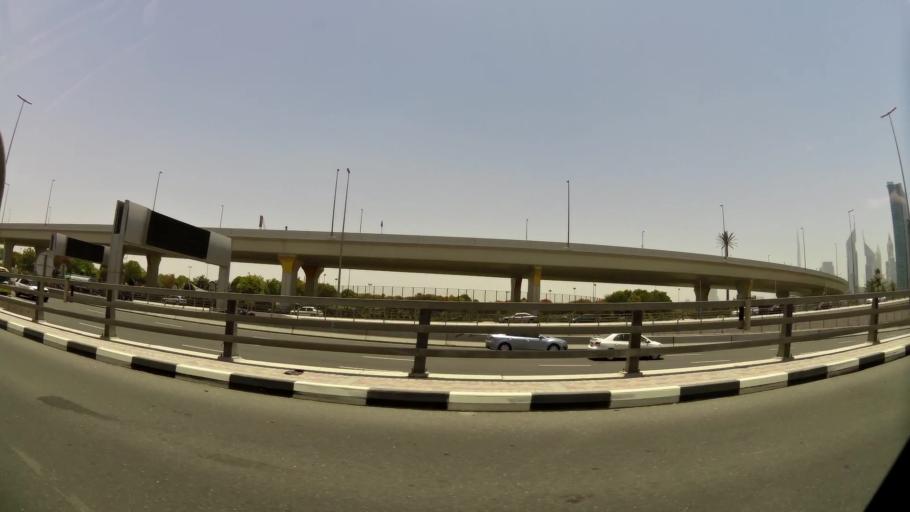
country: AE
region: Ash Shariqah
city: Sharjah
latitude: 25.2308
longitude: 55.2937
